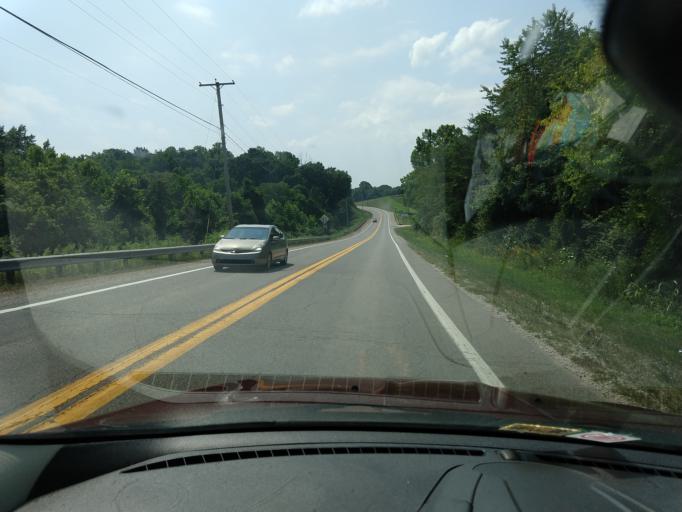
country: US
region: West Virginia
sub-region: Jackson County
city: Ravenswood
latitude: 38.8834
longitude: -81.8358
